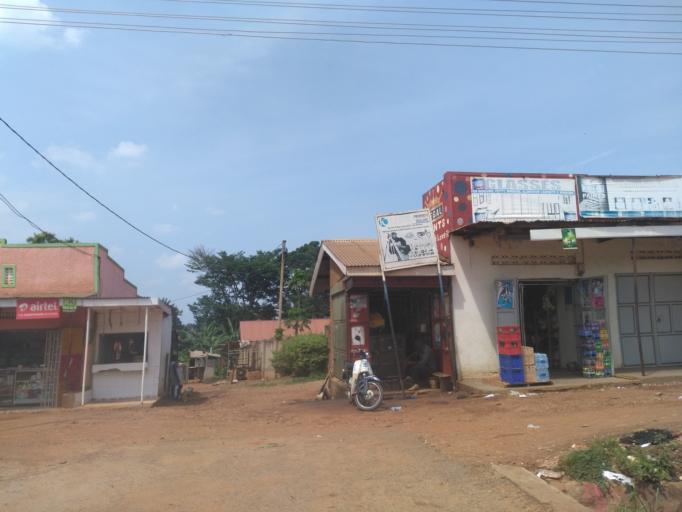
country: UG
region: Central Region
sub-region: Wakiso District
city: Kireka
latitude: 0.4471
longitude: 32.6120
